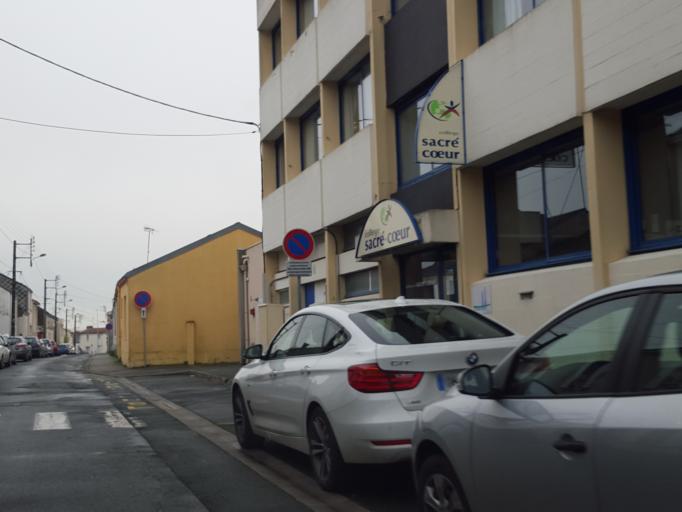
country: FR
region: Pays de la Loire
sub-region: Departement de la Vendee
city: La Roche-sur-Yon
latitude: 46.6775
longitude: -1.4342
